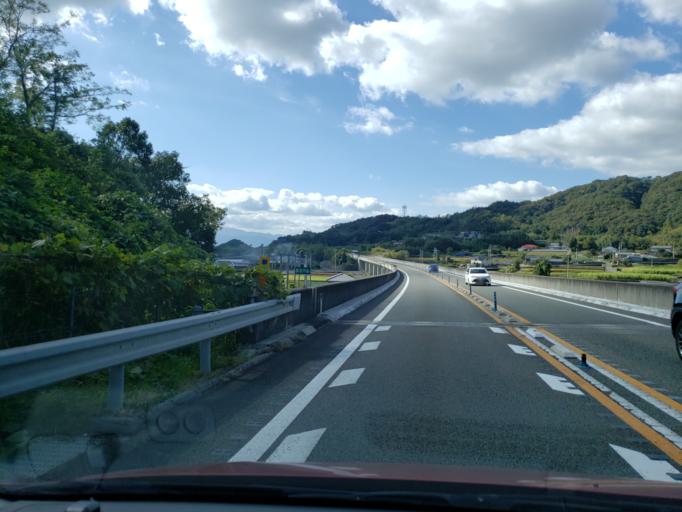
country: JP
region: Tokushima
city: Ishii
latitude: 34.1360
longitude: 134.3972
